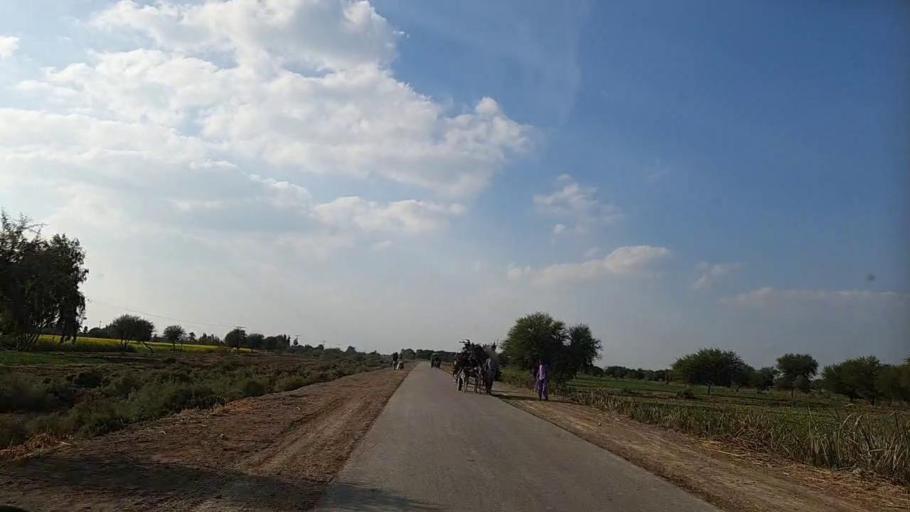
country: PK
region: Sindh
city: Pithoro
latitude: 25.6669
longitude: 69.2379
